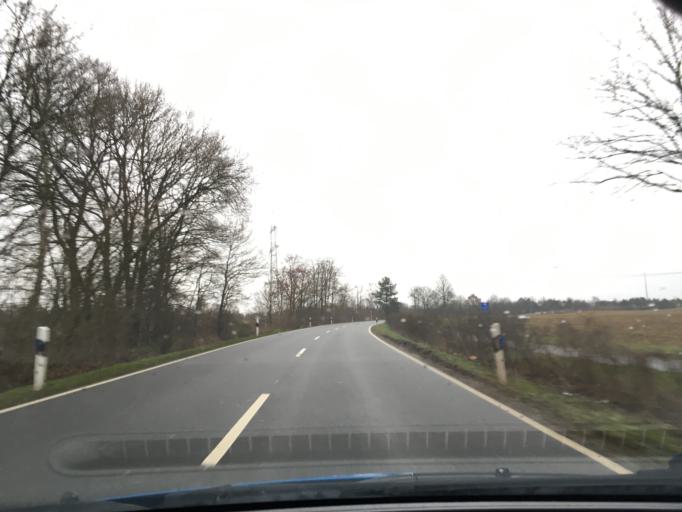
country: DE
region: Schleswig-Holstein
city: Roseburg
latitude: 53.5470
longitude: 10.6397
